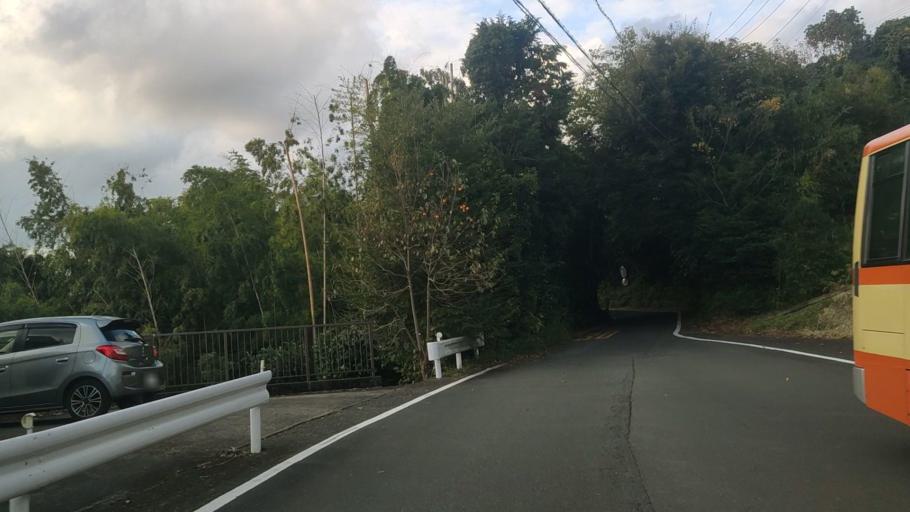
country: JP
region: Shizuoka
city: Ito
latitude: 34.9584
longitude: 139.0797
